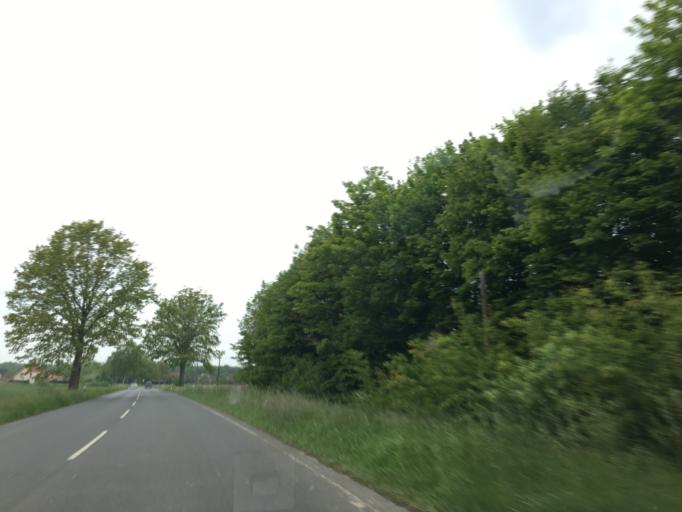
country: DE
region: Lower Saxony
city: Haste
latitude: 52.3801
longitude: 9.4037
